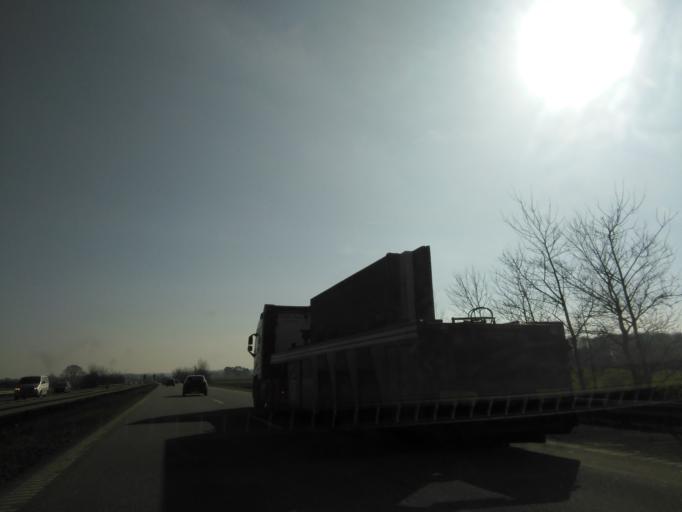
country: DK
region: South Denmark
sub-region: Middelfart Kommune
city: Ejby
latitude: 55.4399
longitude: 9.9727
